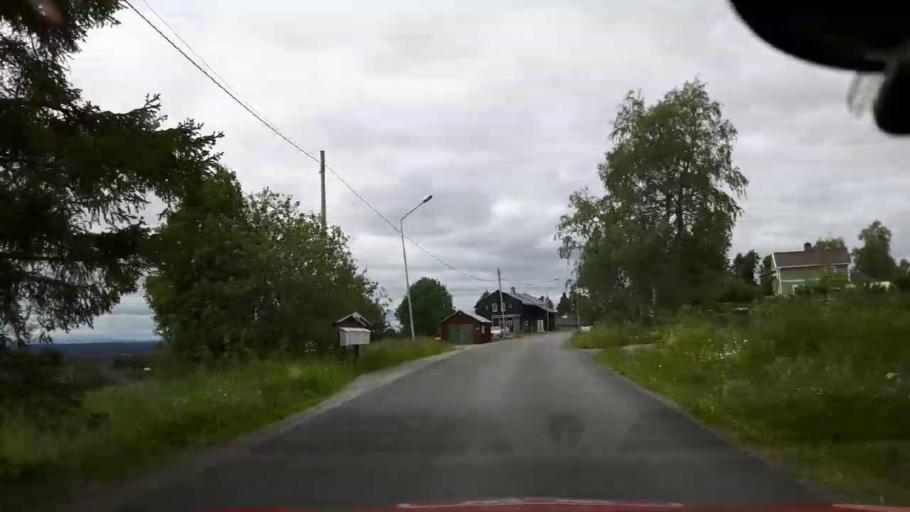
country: SE
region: Jaemtland
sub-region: OEstersunds Kommun
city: Brunflo
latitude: 63.0756
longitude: 14.8827
